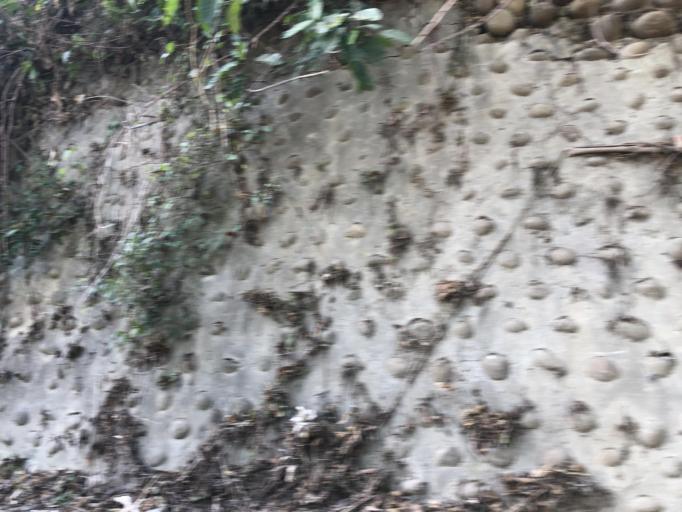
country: TW
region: Taiwan
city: Yujing
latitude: 23.0451
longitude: 120.3981
